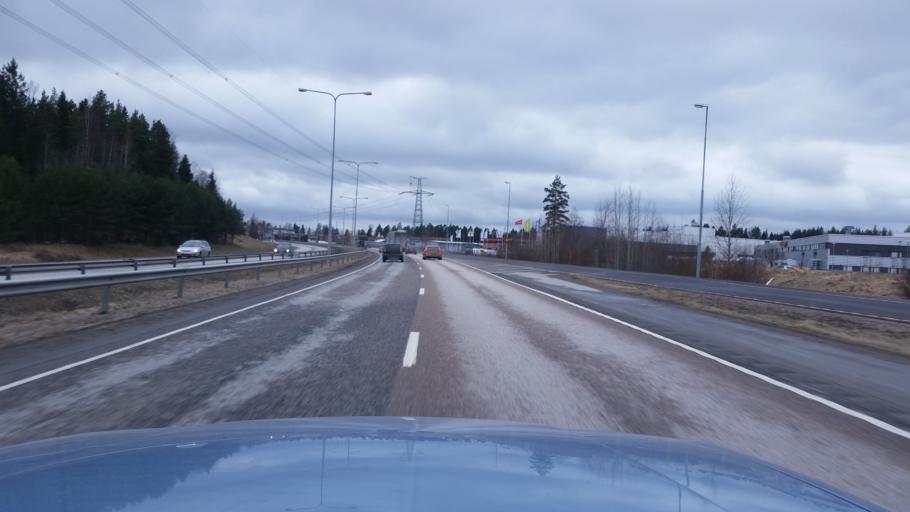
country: FI
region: Uusimaa
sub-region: Helsinki
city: Kauniainen
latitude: 60.2612
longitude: 24.7283
